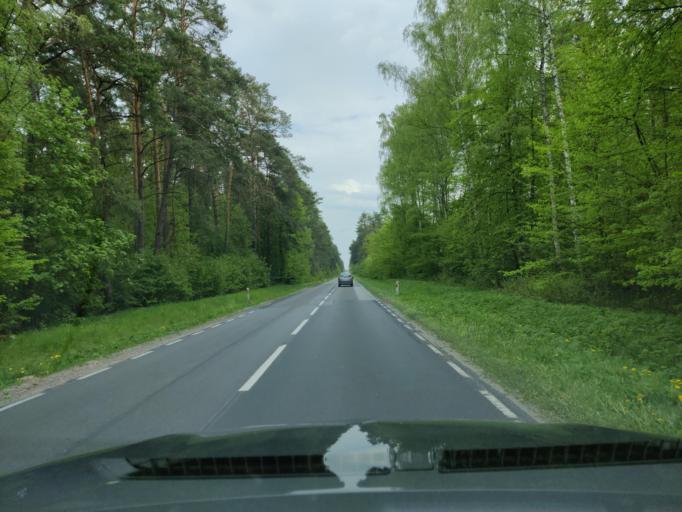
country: PL
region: Masovian Voivodeship
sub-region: Powiat pultuski
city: Obryte
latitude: 52.6416
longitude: 21.2724
